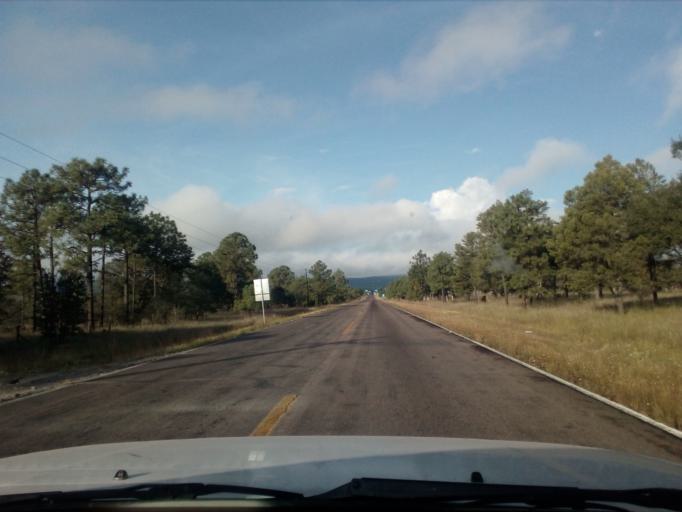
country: MX
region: Durango
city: Victoria de Durango
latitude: 23.9267
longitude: -104.9322
